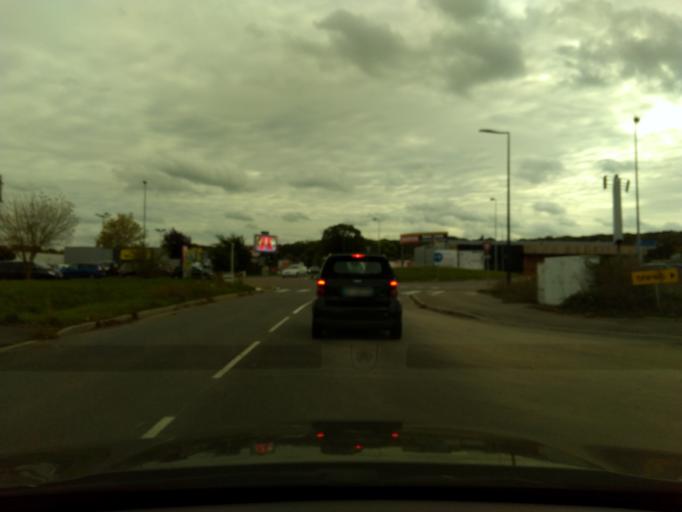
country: FR
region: Lorraine
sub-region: Departement de la Moselle
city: Augny
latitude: 49.0781
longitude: 6.1045
